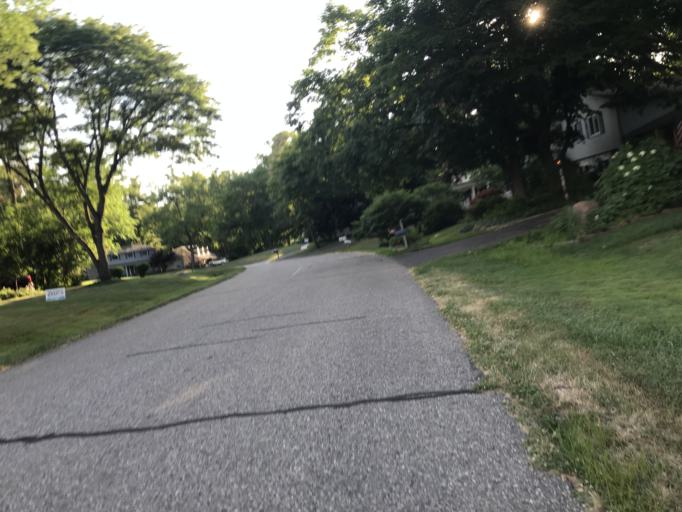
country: US
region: Michigan
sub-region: Oakland County
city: Farmington Hills
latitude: 42.4910
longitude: -83.3457
